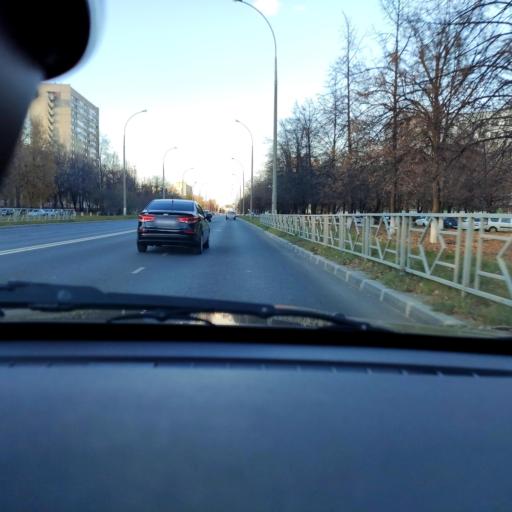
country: RU
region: Samara
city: Tol'yatti
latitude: 53.5218
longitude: 49.3108
